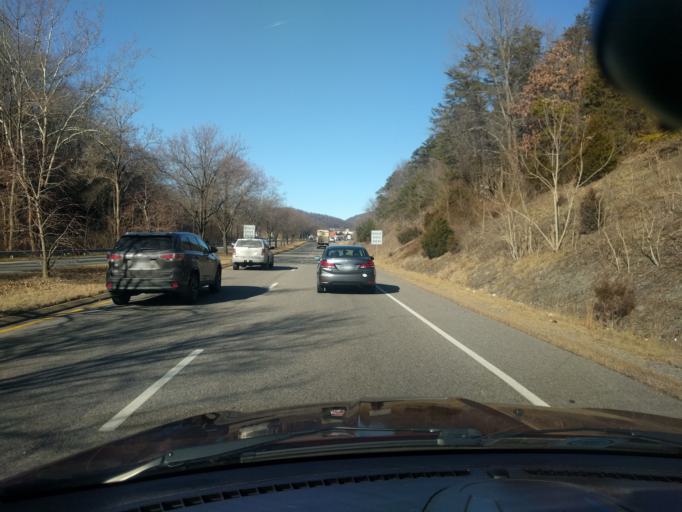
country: US
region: Virginia
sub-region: Augusta County
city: Jolivue
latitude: 38.1230
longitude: -79.0277
